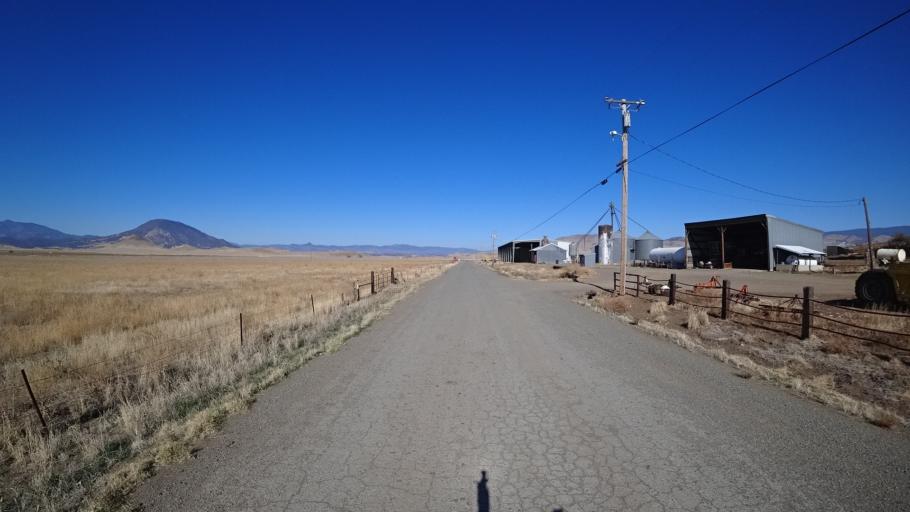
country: US
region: California
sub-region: Siskiyou County
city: Montague
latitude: 41.7911
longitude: -122.4343
